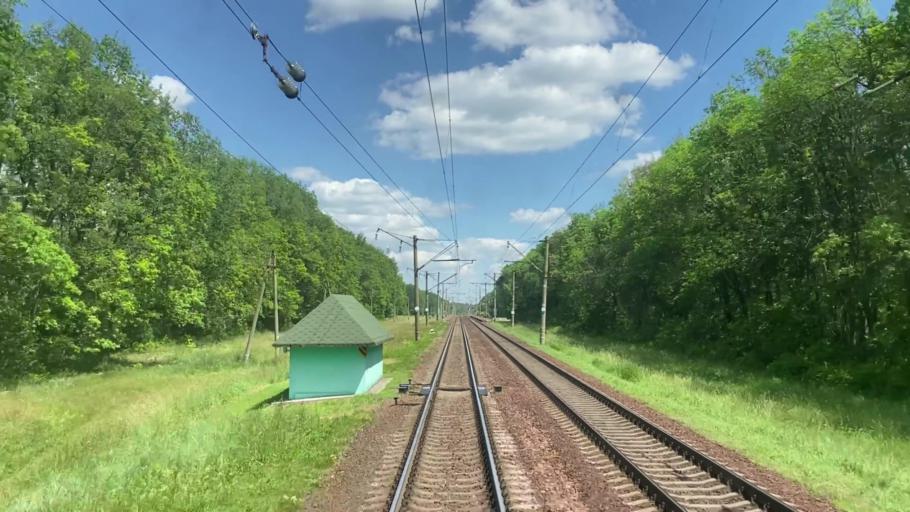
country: BY
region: Brest
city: Pruzhany
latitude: 52.4967
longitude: 24.6075
